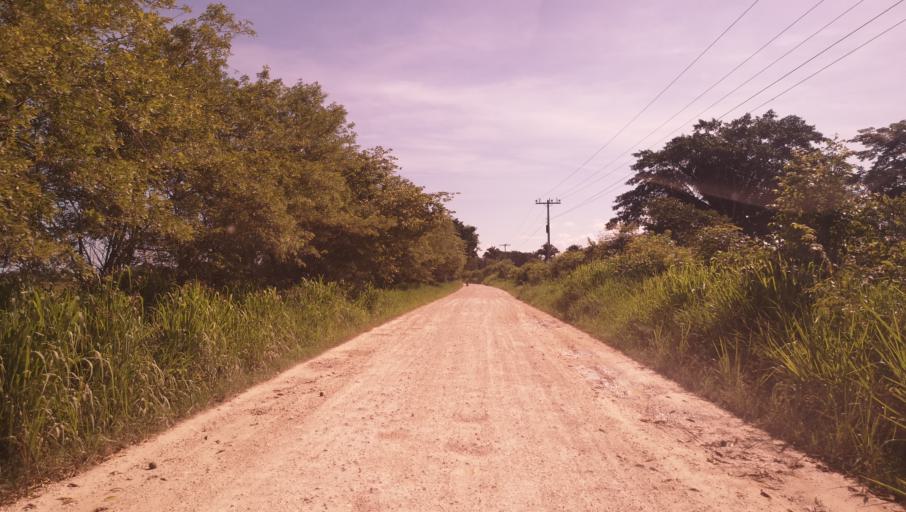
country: GT
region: Peten
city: Dolores
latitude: 16.7180
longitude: -89.3622
